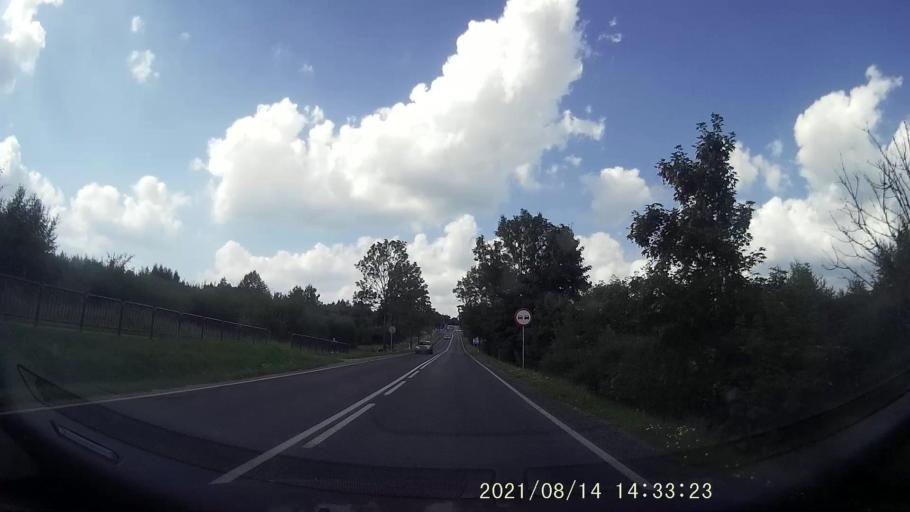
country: PL
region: Lower Silesian Voivodeship
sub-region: Powiat klodzki
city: Nowa Ruda
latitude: 50.5579
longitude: 16.5435
